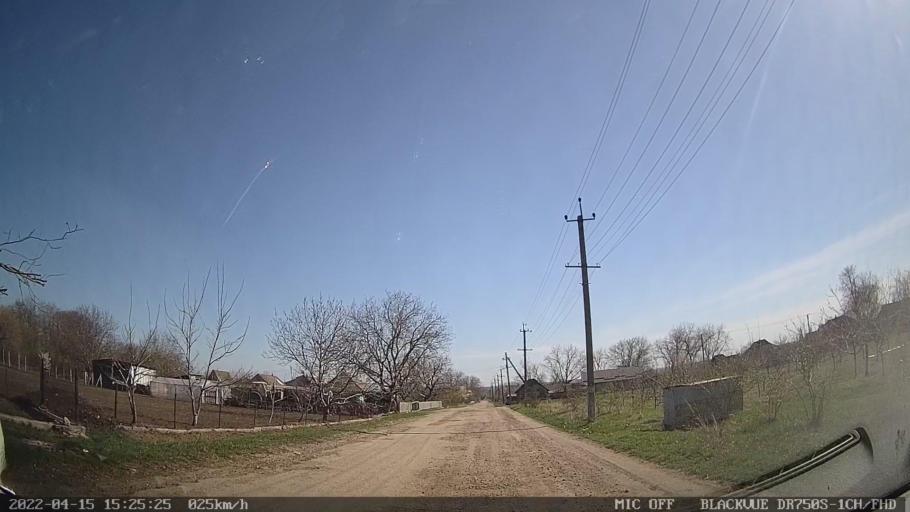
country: MD
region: Raionul Ocnita
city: Otaci
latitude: 48.3651
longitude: 27.9263
